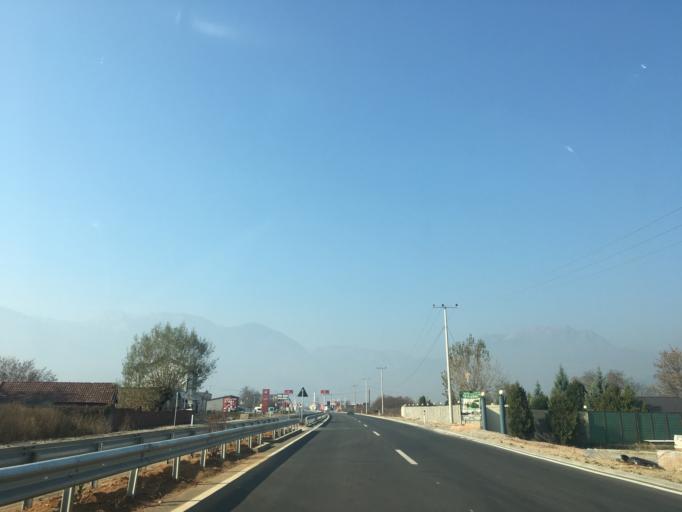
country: XK
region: Pec
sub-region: Komuna e Pejes
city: Dubova (Driloni)
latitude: 42.6584
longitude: 20.3477
